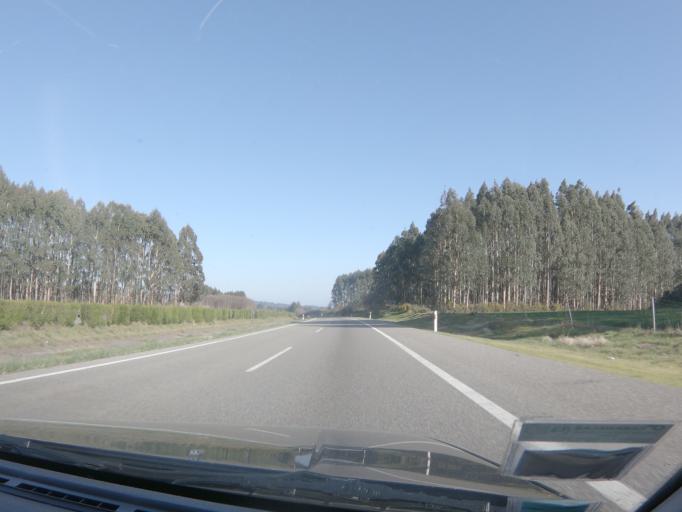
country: ES
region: Galicia
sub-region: Provincia de Lugo
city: Guitiriz
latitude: 43.1892
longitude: -7.8614
